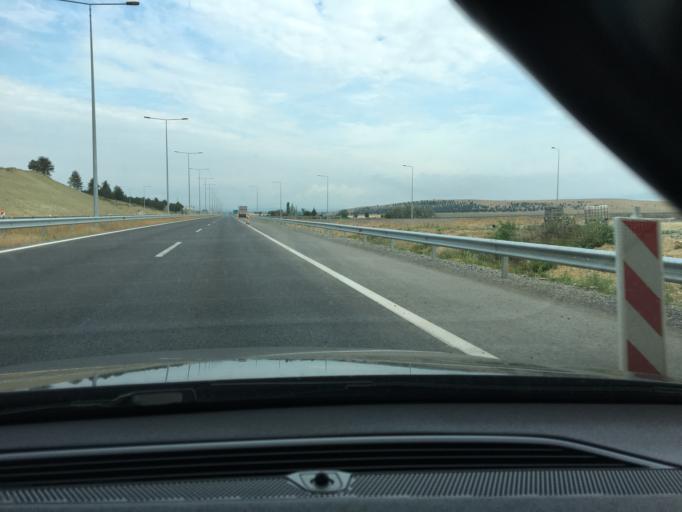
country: MK
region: Stip
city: Shtip
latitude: 41.7821
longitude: 22.1253
